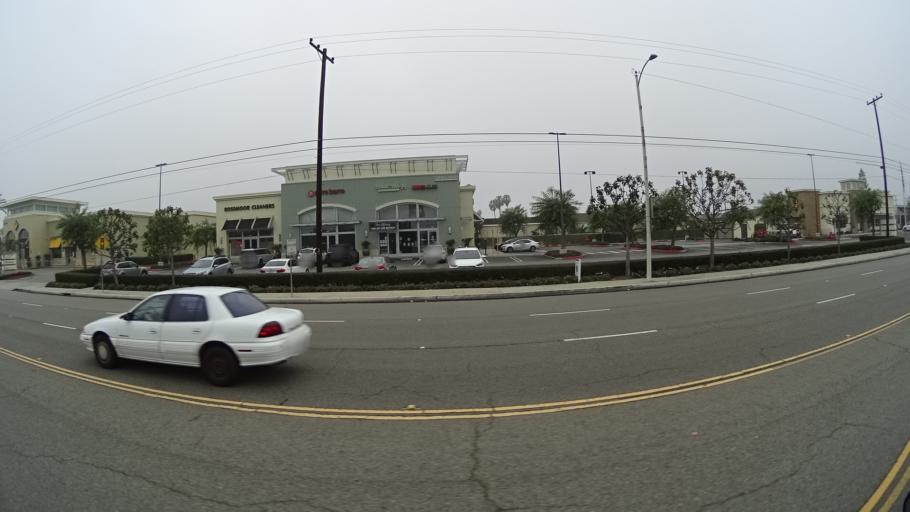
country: US
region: California
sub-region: Orange County
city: Rossmoor
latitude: 33.7866
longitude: -118.0729
